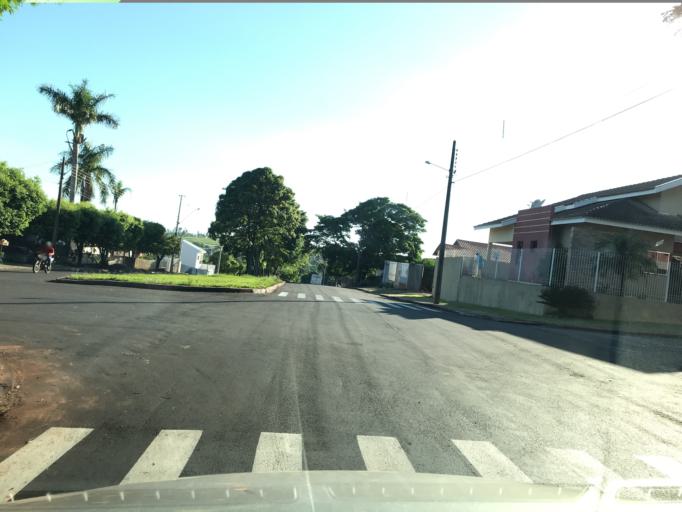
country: BR
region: Parana
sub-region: Ipora
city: Ipora
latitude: -24.0004
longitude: -53.7128
